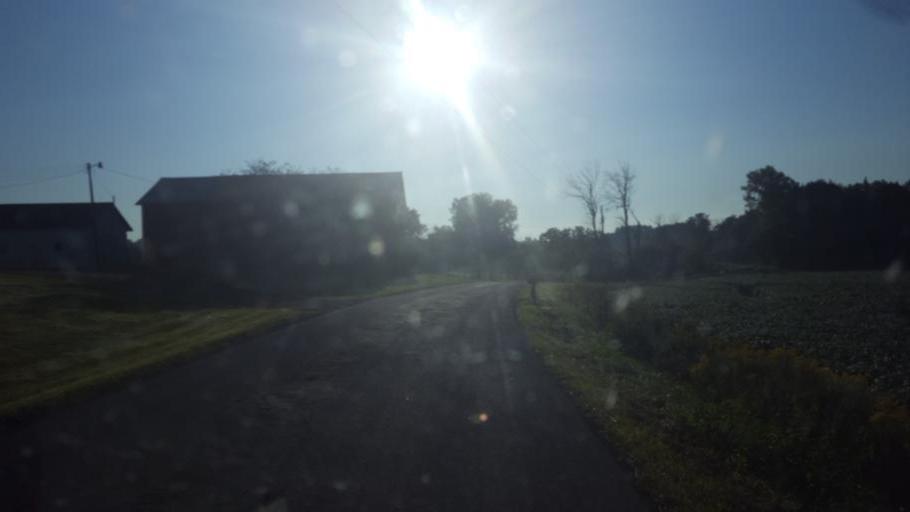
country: US
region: Ohio
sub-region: Morrow County
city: Mount Gilead
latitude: 40.5386
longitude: -82.7637
